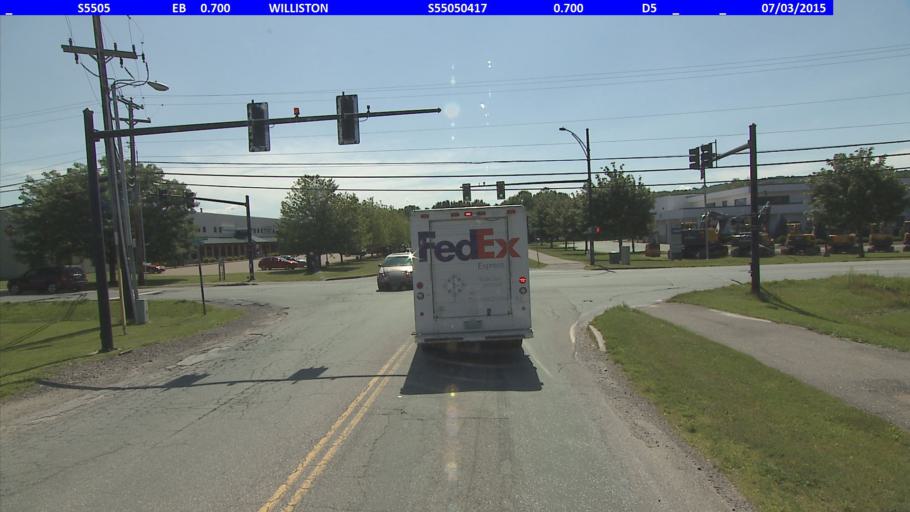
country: US
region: Vermont
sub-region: Chittenden County
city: South Burlington
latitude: 44.4456
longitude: -73.1290
